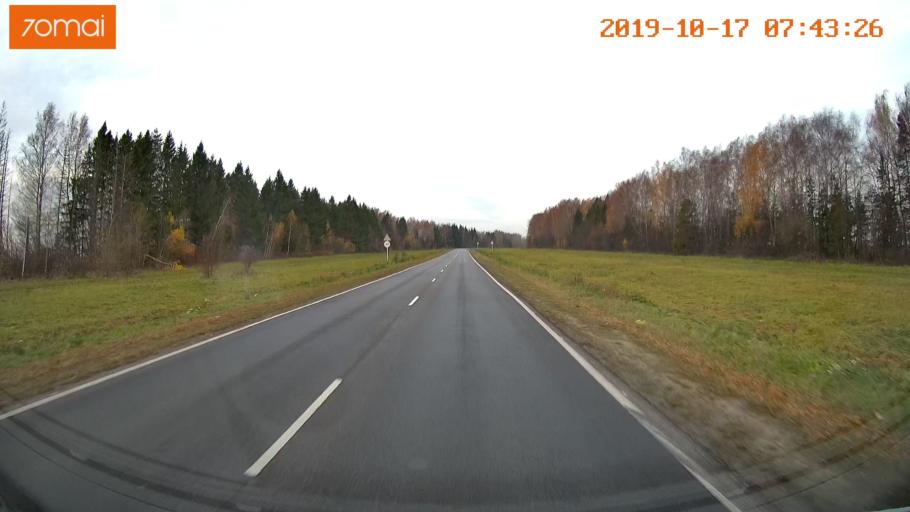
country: RU
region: Vladimir
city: Yur'yev-Pol'skiy
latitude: 56.4826
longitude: 39.7648
